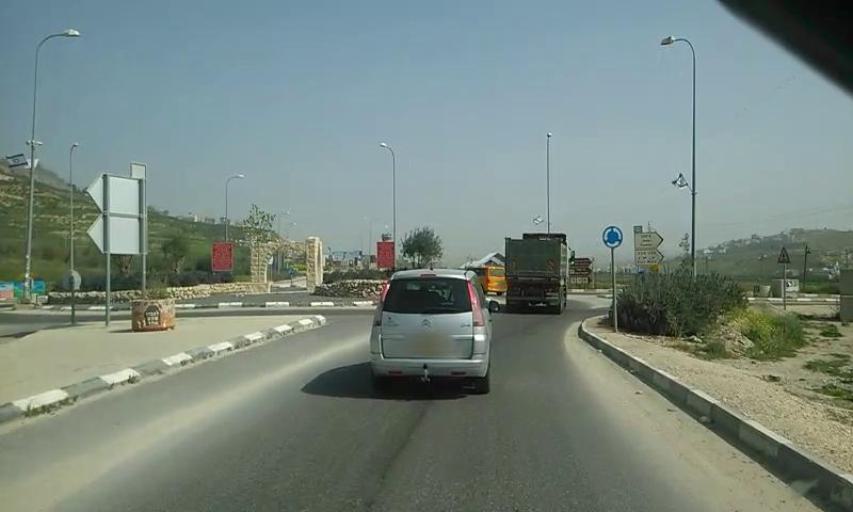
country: PS
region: West Bank
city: `Awarta
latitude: 32.1761
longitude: 35.2726
